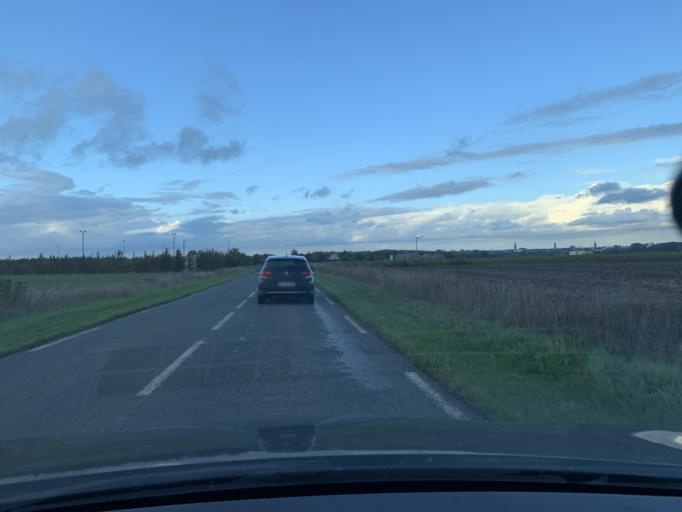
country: FR
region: Nord-Pas-de-Calais
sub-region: Departement du Nord
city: Proville
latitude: 50.1504
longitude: 3.2105
